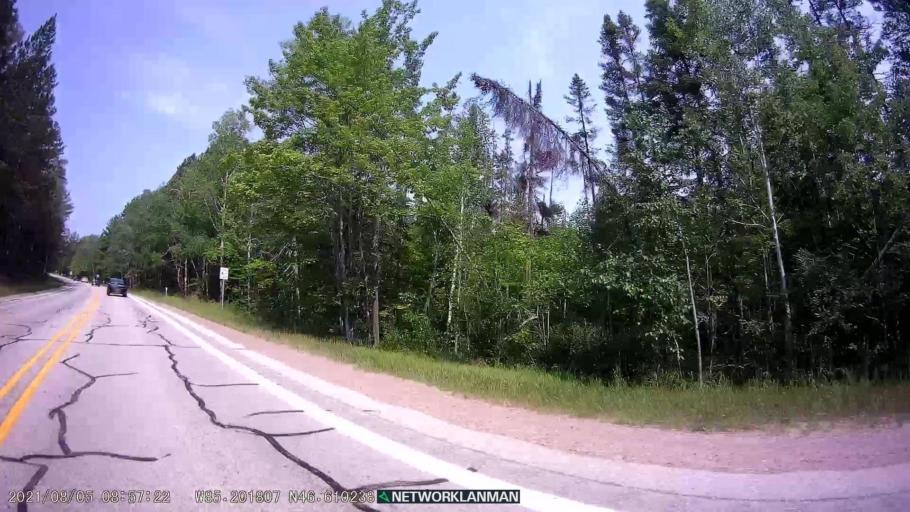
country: US
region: Michigan
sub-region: Luce County
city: Newberry
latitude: 46.6103
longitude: -85.2020
